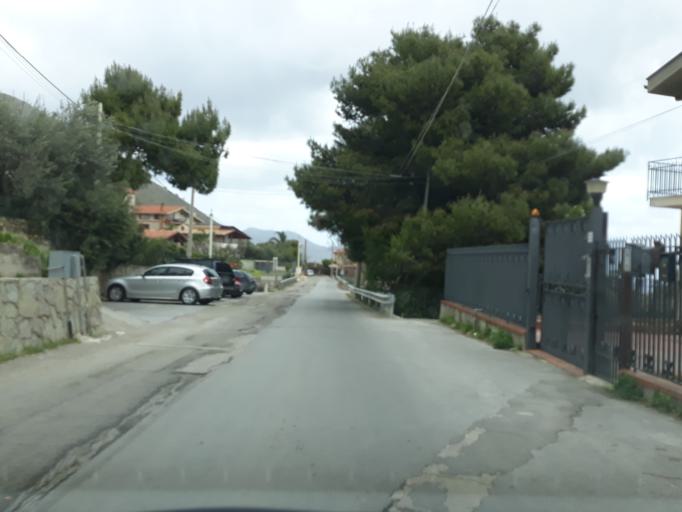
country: IT
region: Sicily
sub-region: Palermo
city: Monreale
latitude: 38.0813
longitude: 13.2967
